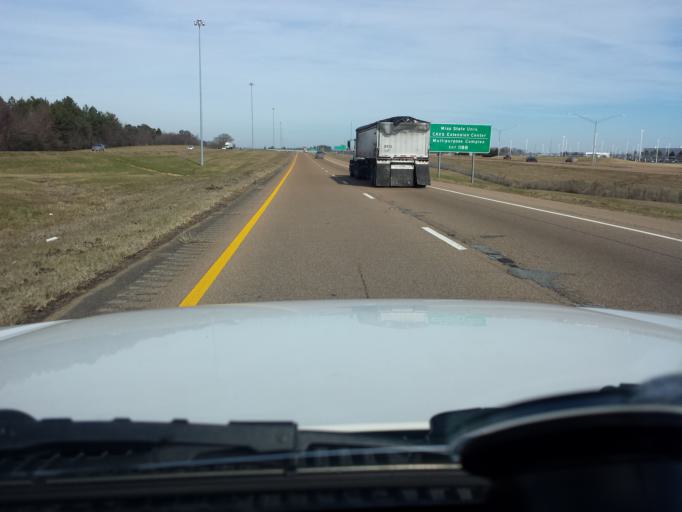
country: US
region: Mississippi
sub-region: Madison County
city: Canton
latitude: 32.5716
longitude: -90.0746
